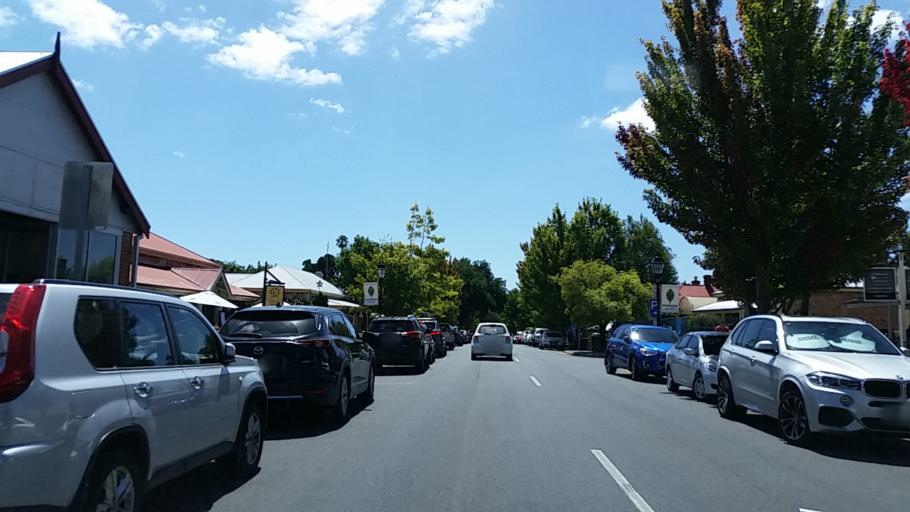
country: AU
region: South Australia
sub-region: Mount Barker
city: Hahndorf
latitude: -35.0325
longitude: 138.8121
